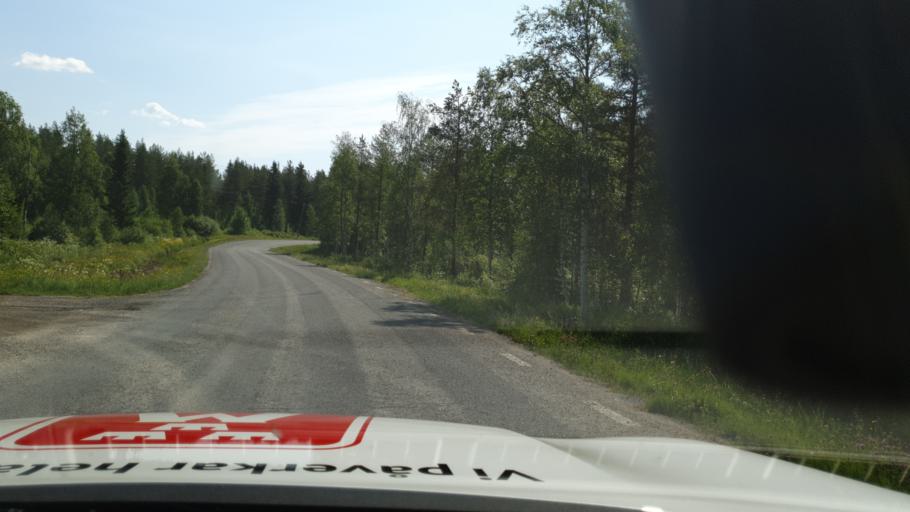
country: SE
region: Vaesterbotten
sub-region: Skelleftea Kommun
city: Langsele
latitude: 65.0114
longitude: 20.0833
